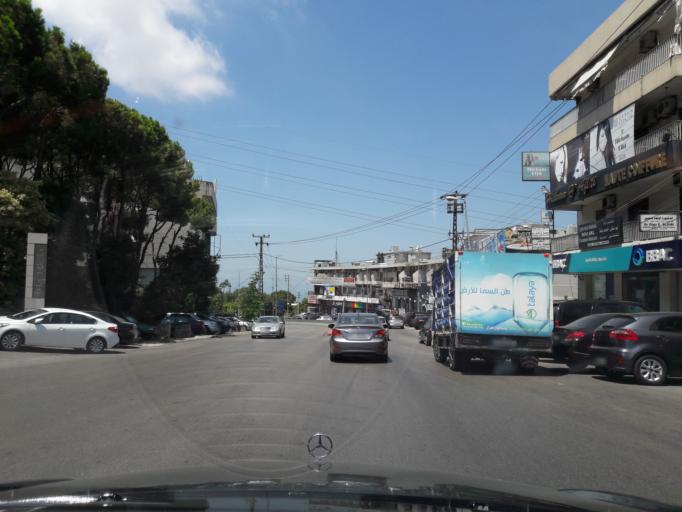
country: LB
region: Mont-Liban
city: Djounie
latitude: 33.9272
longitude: 35.6275
